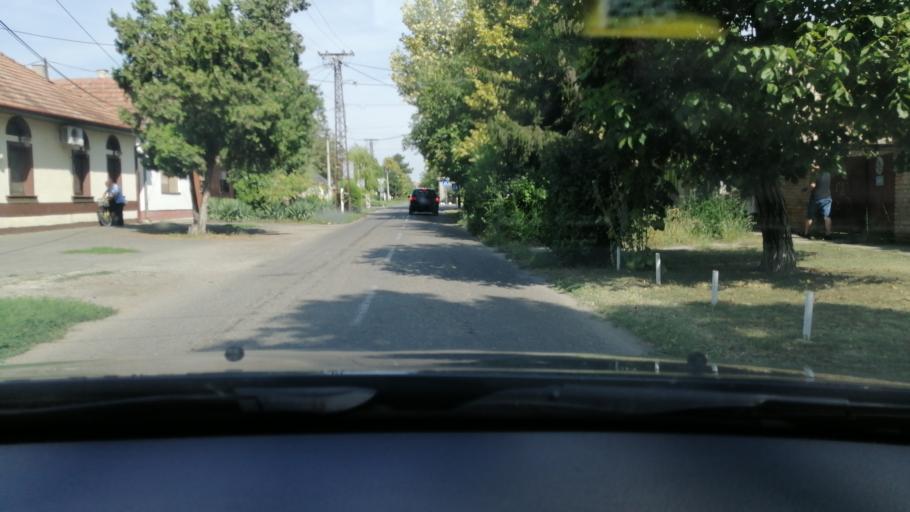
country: RS
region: Autonomna Pokrajina Vojvodina
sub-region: Srednjebanatski Okrug
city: Zrenjanin
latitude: 45.3868
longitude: 20.3770
